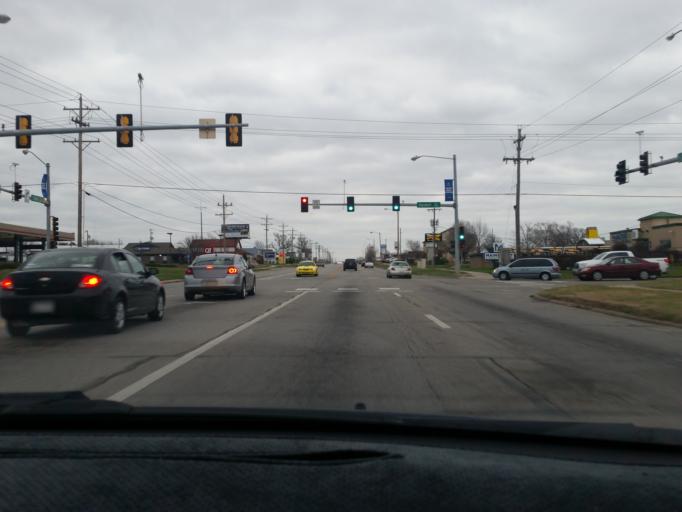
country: US
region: Kansas
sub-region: Douglas County
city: Lawrence
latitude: 38.9427
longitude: -95.2238
